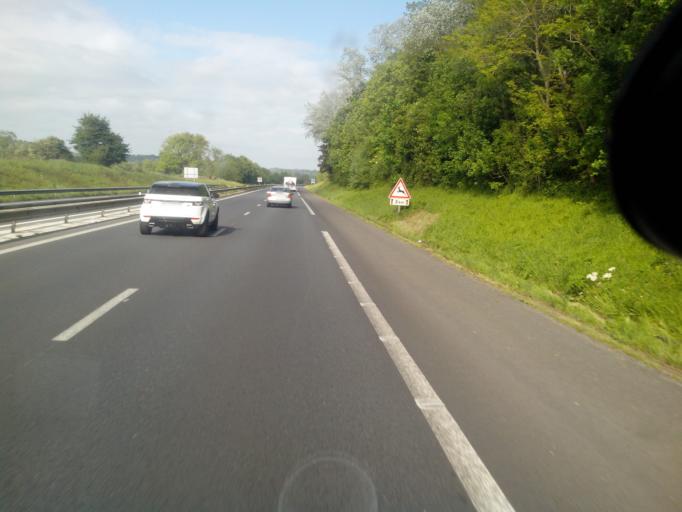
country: FR
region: Lower Normandy
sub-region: Departement du Calvados
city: Dozule
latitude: 49.2379
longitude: -0.0391
